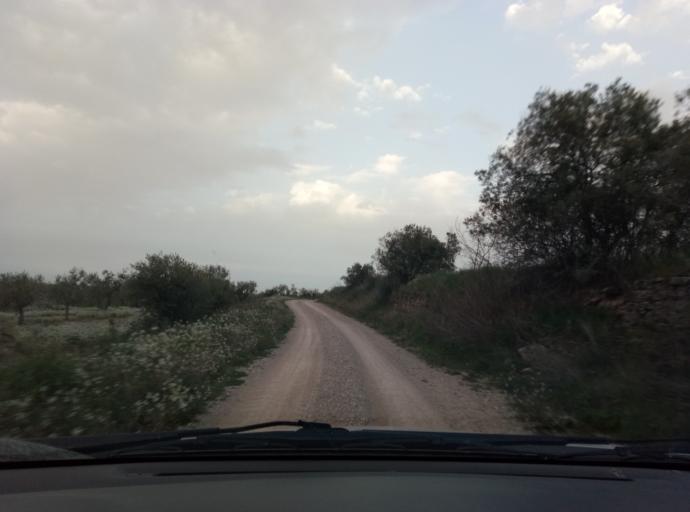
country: ES
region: Catalonia
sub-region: Provincia de Lleida
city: Ciutadilla
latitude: 41.5726
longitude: 1.1572
